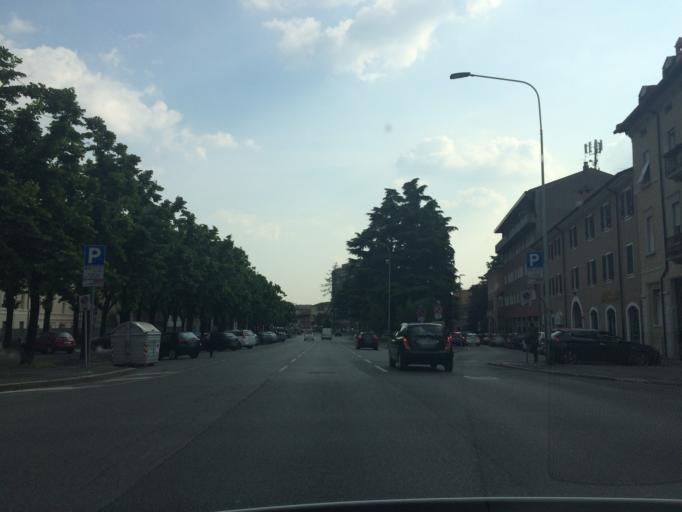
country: IT
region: Lombardy
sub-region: Provincia di Brescia
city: Brescia
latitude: 45.5433
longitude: 10.2116
